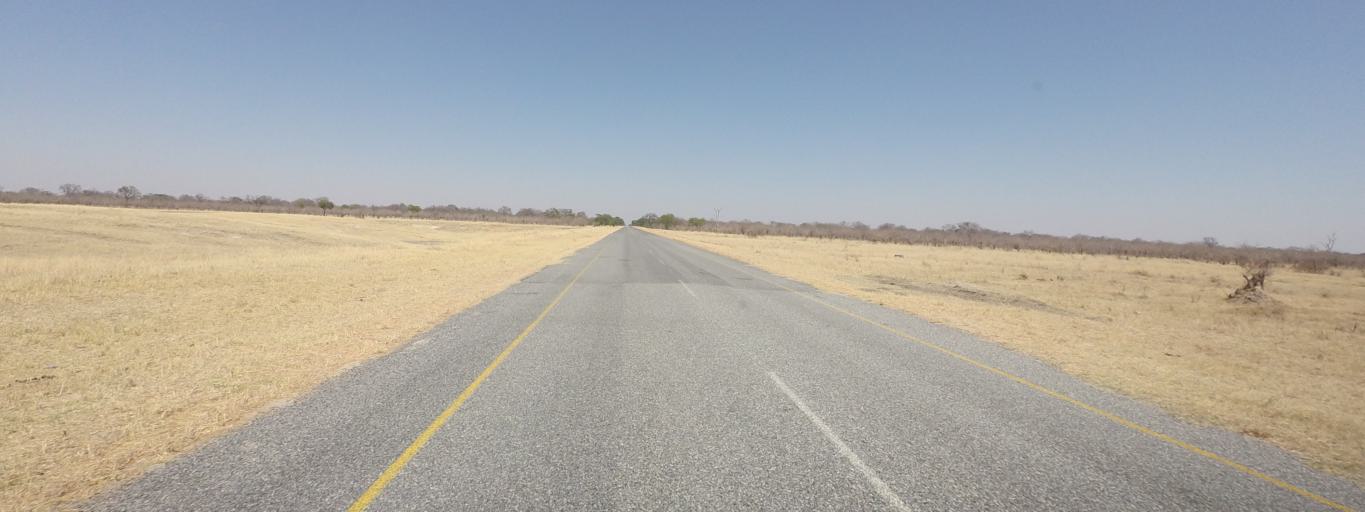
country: BW
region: North West
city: Kasane
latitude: -17.9220
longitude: 24.9347
